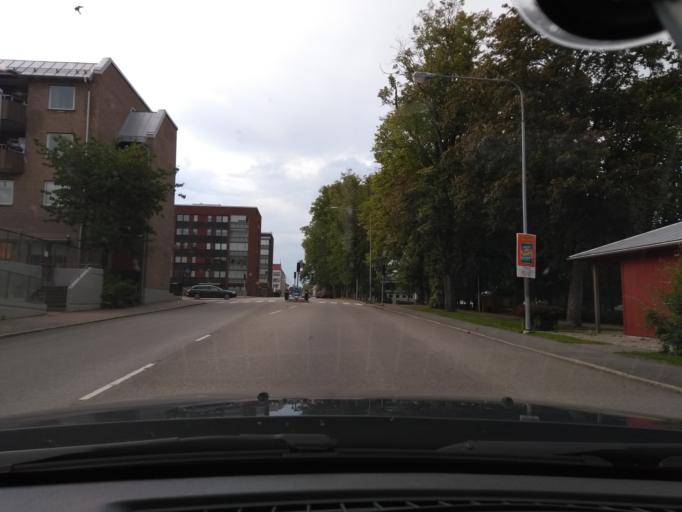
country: SE
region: Joenkoeping
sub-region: Nassjo Kommun
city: Nassjo
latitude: 57.6523
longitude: 14.7004
